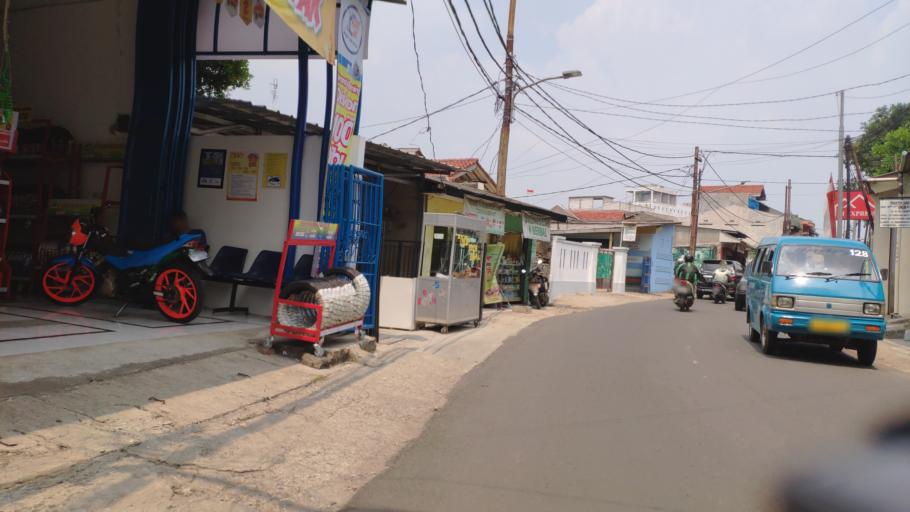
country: ID
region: West Java
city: Depok
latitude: -6.3451
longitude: 106.8312
